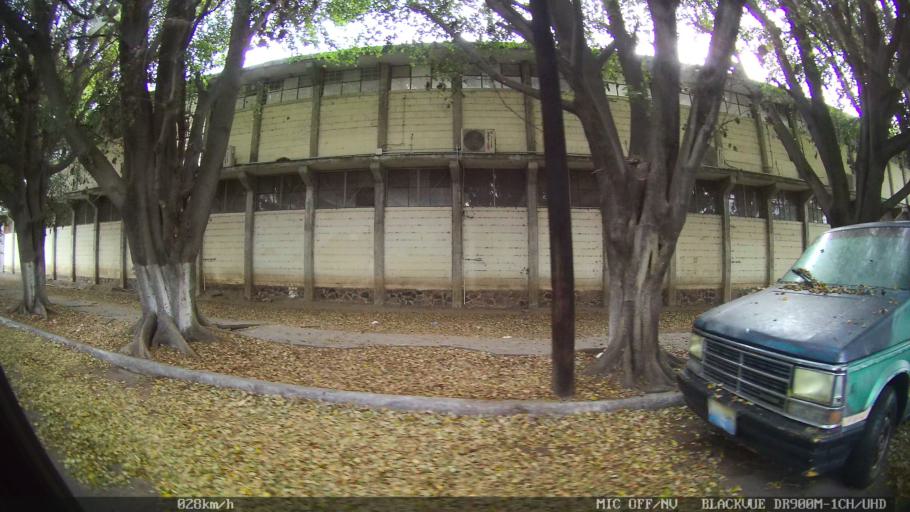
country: MX
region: Jalisco
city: Guadalajara
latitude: 20.6593
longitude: -103.4041
